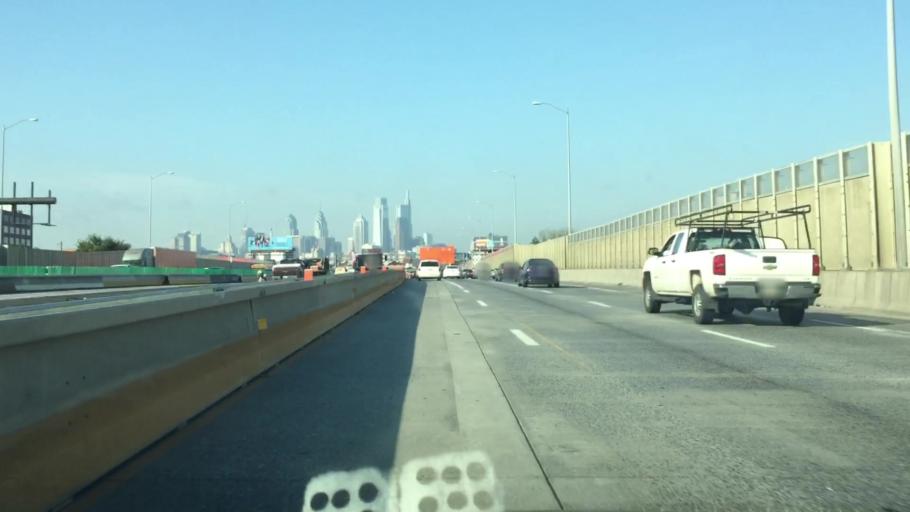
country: US
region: Pennsylvania
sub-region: Philadelphia County
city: Philadelphia
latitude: 39.9683
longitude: -75.1299
